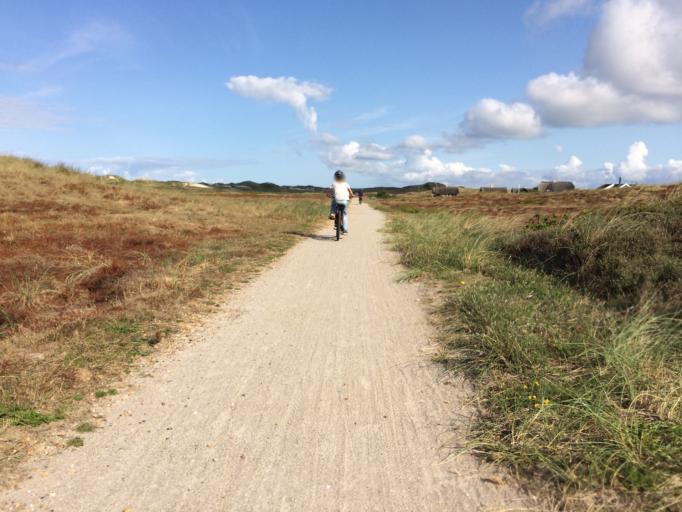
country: DK
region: Central Jutland
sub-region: Ringkobing-Skjern Kommune
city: Hvide Sande
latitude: 55.9044
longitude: 8.1571
